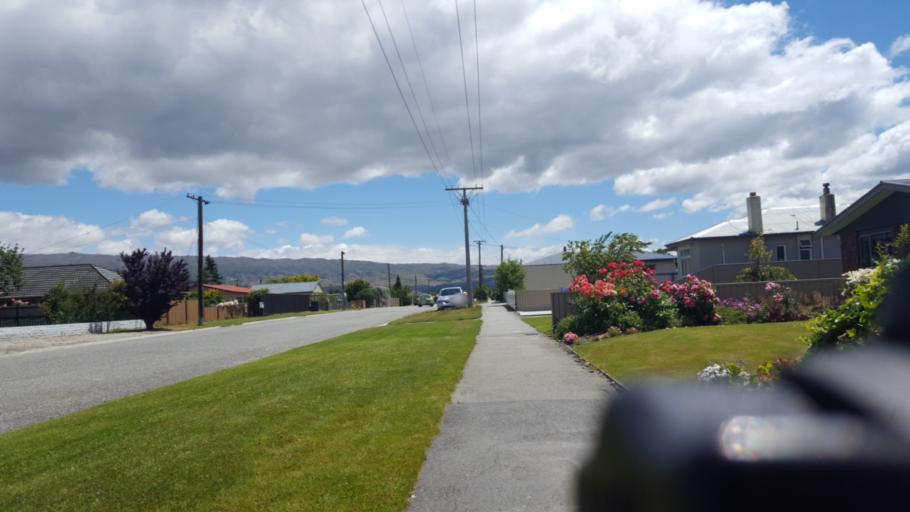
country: NZ
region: Otago
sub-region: Queenstown-Lakes District
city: Wanaka
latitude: -45.2487
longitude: 169.3916
